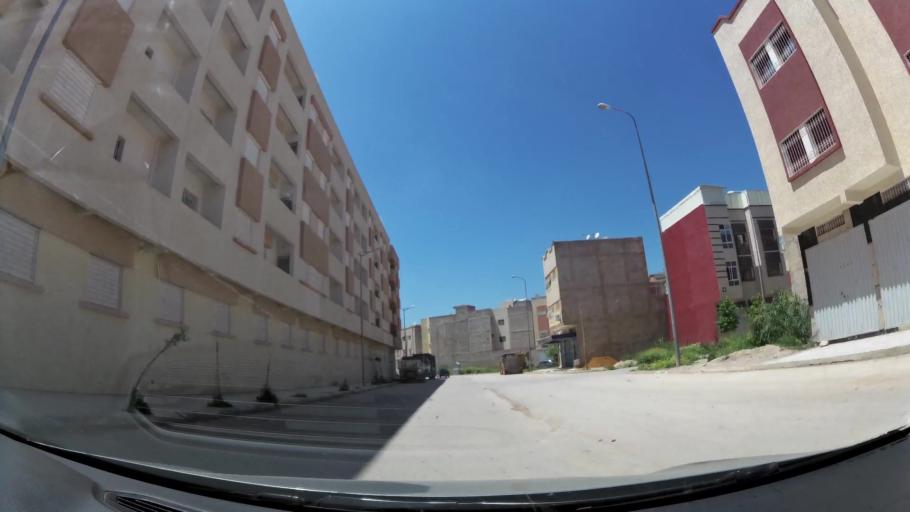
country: MA
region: Fes-Boulemane
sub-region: Fes
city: Fes
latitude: 34.0303
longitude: -5.0482
